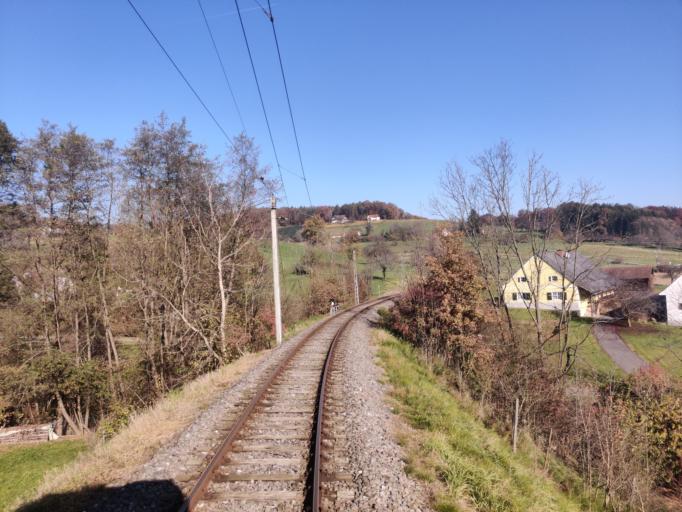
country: AT
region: Styria
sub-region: Politischer Bezirk Suedoststeiermark
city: Feldbach
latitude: 46.9347
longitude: 15.8658
